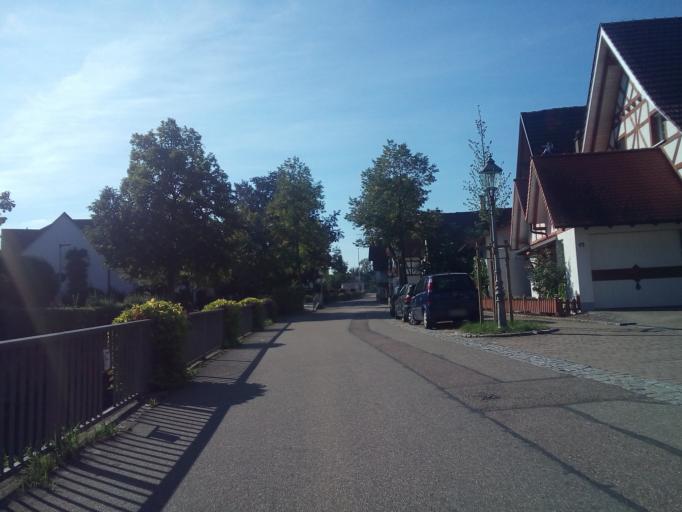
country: DE
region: Baden-Wuerttemberg
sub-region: Freiburg Region
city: Sasbach
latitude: 48.6400
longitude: 8.0944
